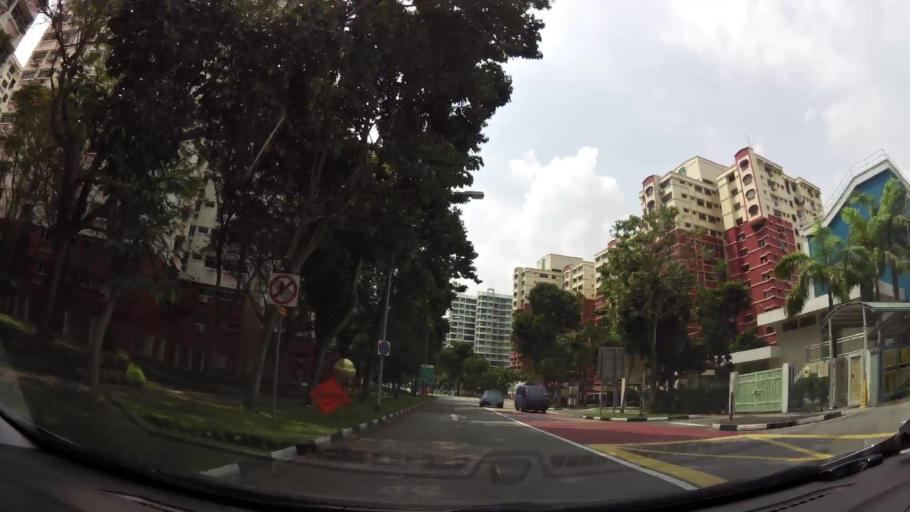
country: MY
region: Johor
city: Kampung Pasir Gudang Baru
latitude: 1.3744
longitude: 103.9458
